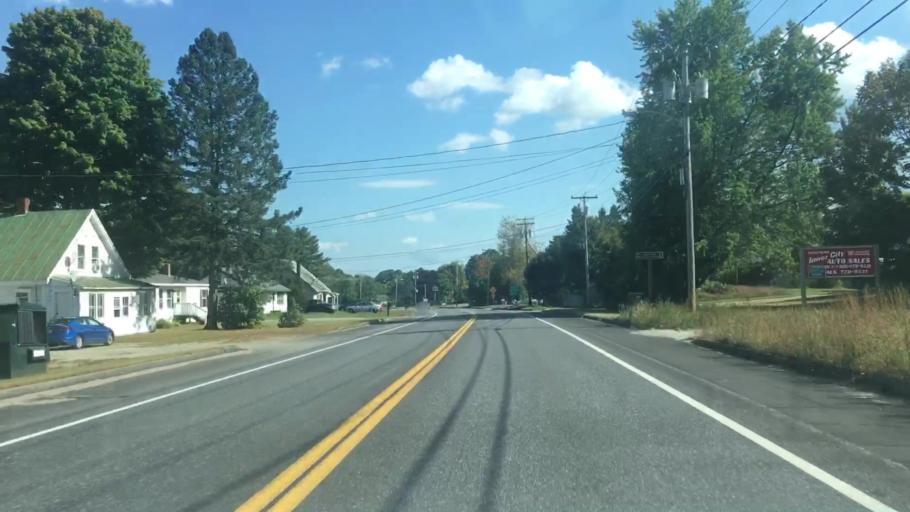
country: US
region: Maine
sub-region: Franklin County
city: Farmington
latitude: 44.6549
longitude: -70.1356
